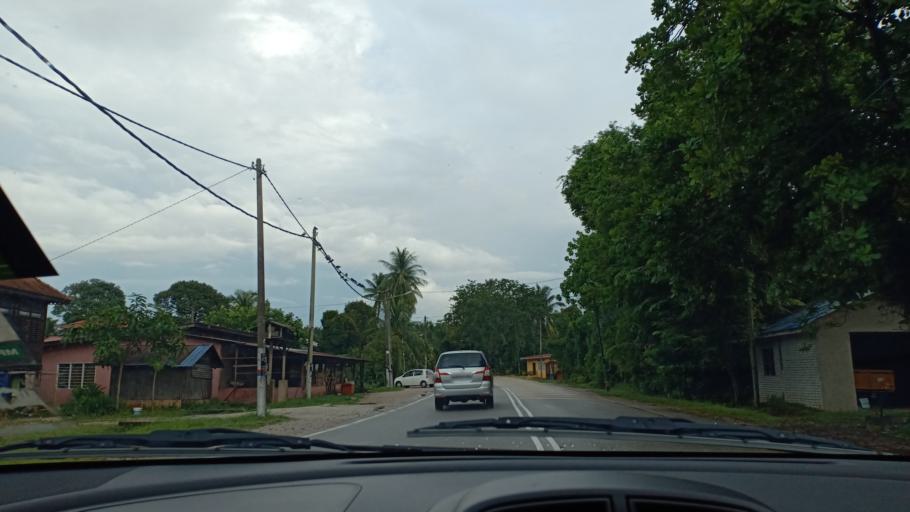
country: MY
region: Penang
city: Tasek Glugor
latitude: 5.4490
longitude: 100.4812
